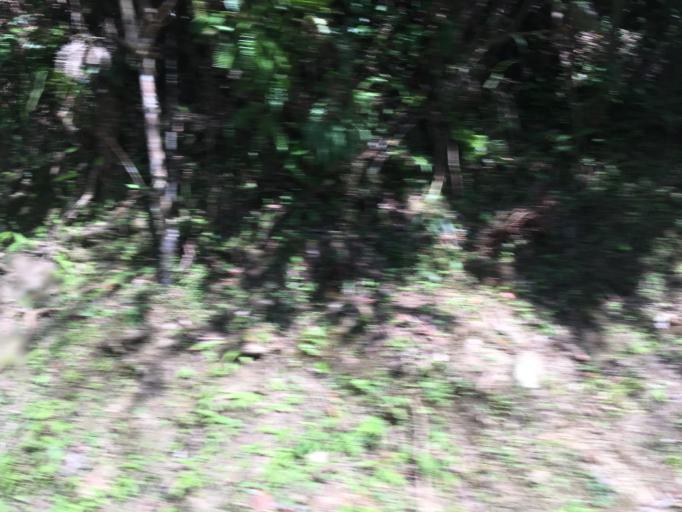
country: TW
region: Taiwan
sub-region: Yilan
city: Yilan
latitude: 24.7566
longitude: 121.6194
